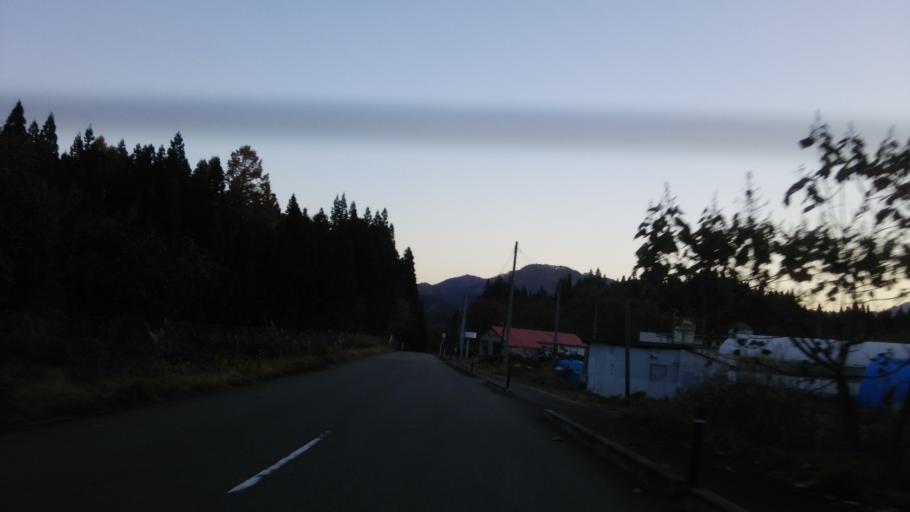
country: JP
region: Fukushima
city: Kitakata
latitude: 37.4854
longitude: 139.6620
